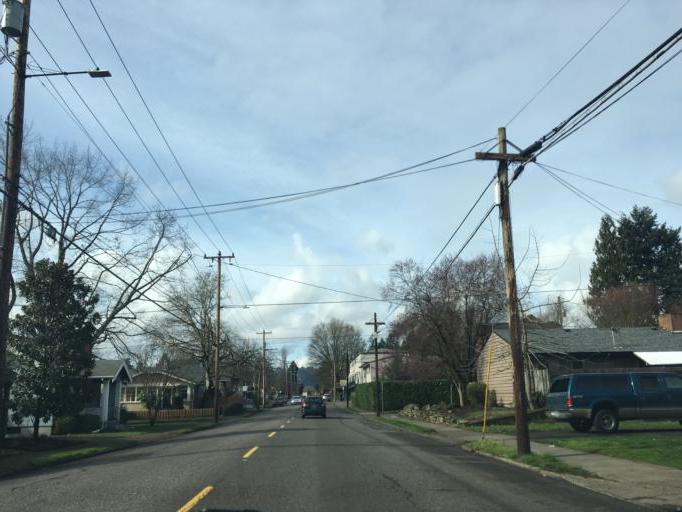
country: US
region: Oregon
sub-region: Clackamas County
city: Milwaukie
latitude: 45.4904
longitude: -122.6249
